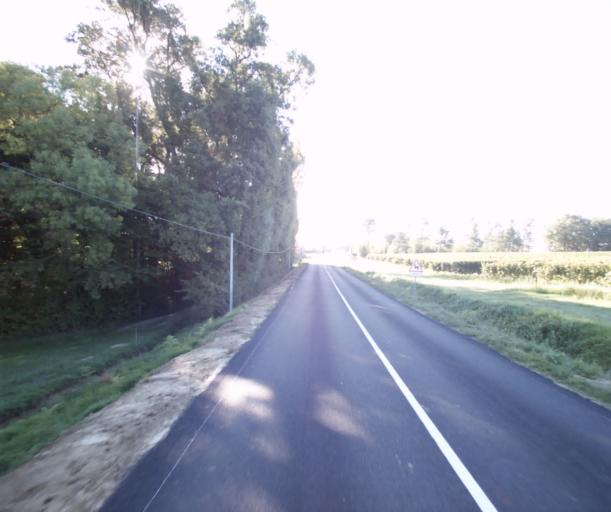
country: FR
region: Midi-Pyrenees
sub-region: Departement du Gers
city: Cazaubon
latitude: 43.8938
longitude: -0.0093
